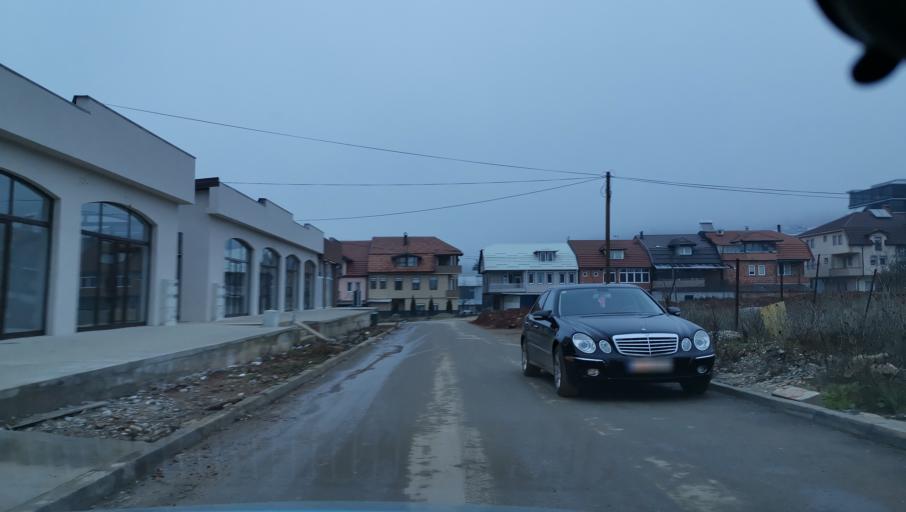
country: MK
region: Debar
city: Debar
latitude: 41.5180
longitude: 20.5273
